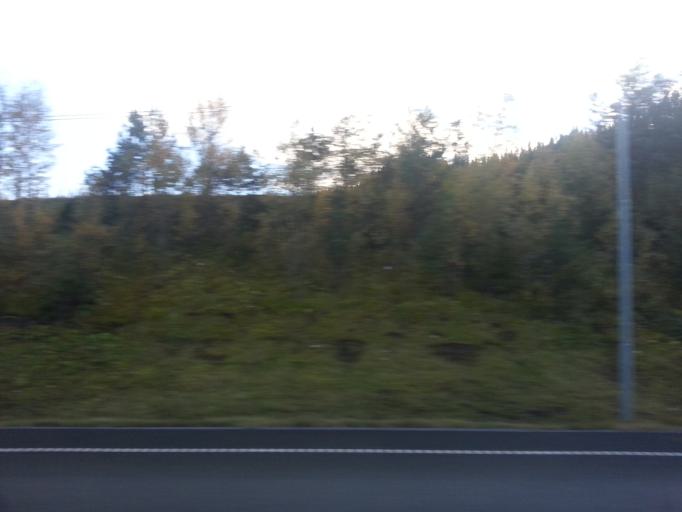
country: NO
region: Sor-Trondelag
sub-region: Malvik
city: Malvik
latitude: 63.4203
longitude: 10.7372
